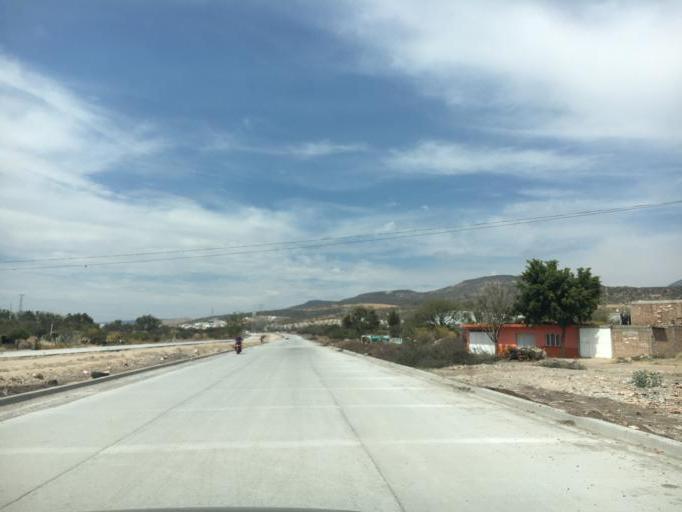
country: MX
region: Guanajuato
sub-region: Leon
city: Fraccionamiento Paraiso Real
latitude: 21.1171
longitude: -101.5906
